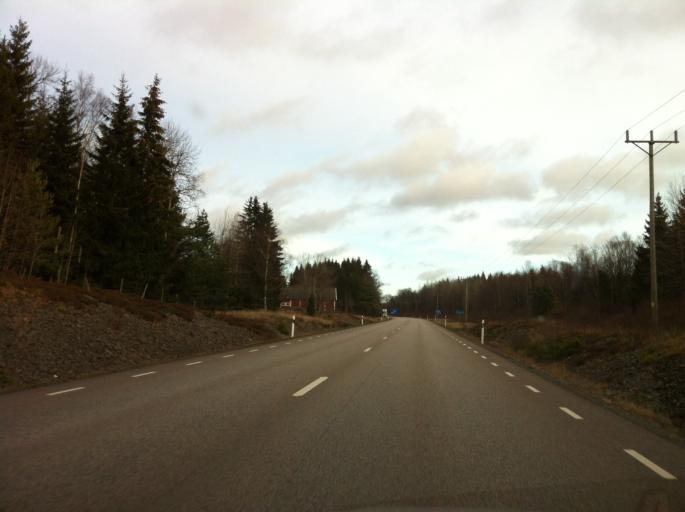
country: SE
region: Kronoberg
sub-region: Uppvidinge Kommun
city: Aseda
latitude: 57.1256
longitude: 15.2670
